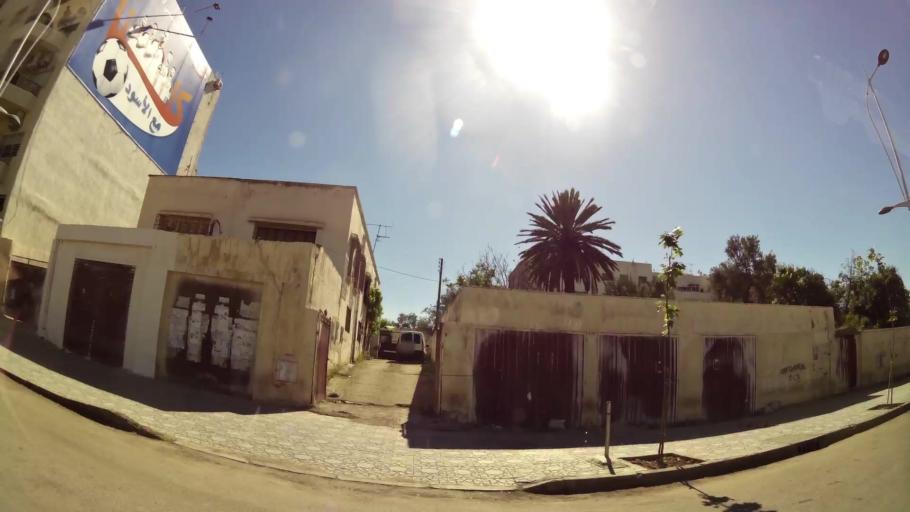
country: MA
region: Fes-Boulemane
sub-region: Fes
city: Fes
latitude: 34.0275
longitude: -4.9916
